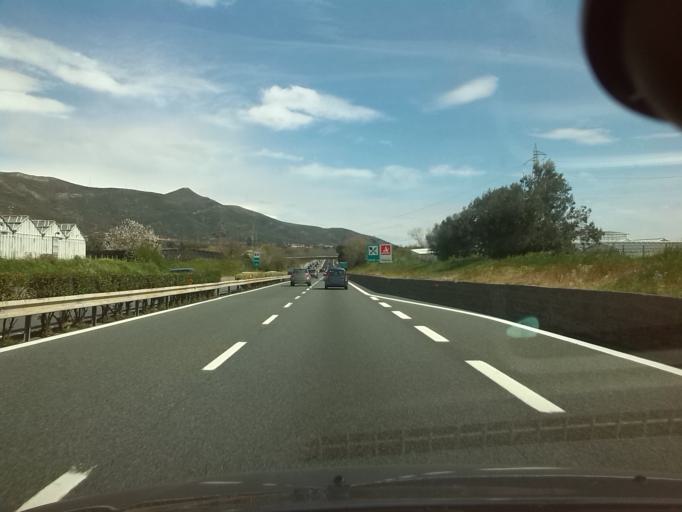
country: IT
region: Liguria
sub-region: Provincia di Savona
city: Campochiesa
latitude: 44.0721
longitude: 8.1832
